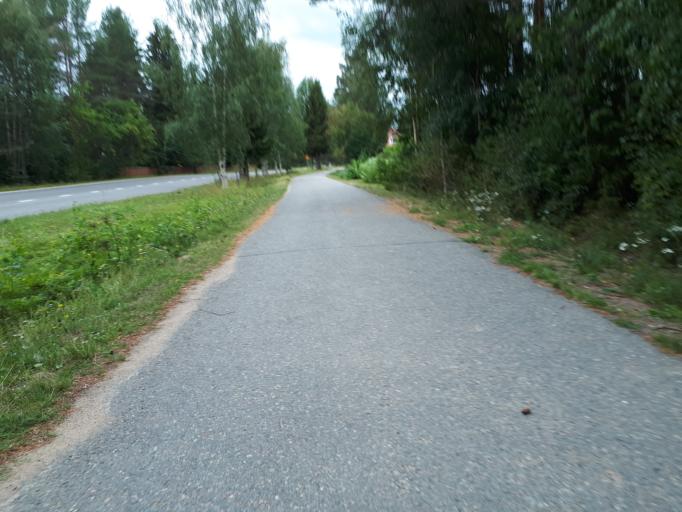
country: FI
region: Northern Ostrobothnia
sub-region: Oulunkaari
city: Ii
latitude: 65.3162
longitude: 25.3950
